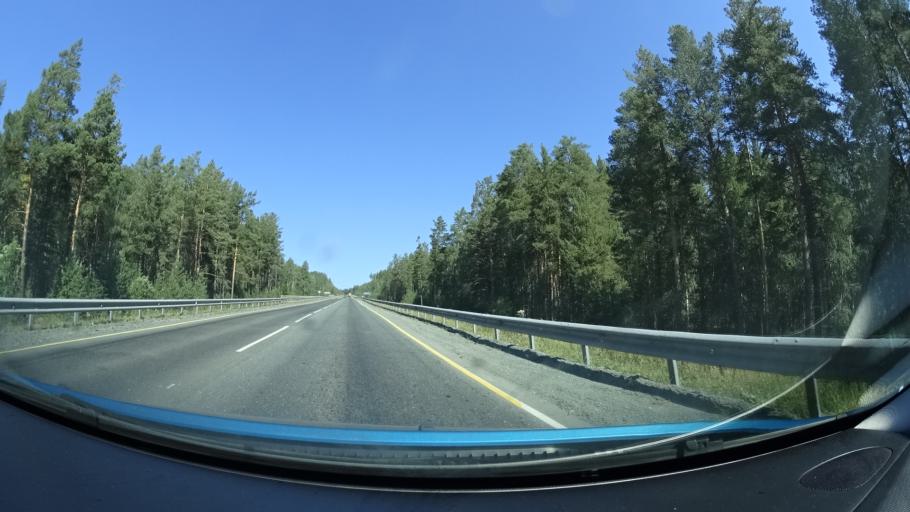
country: RU
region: Bashkortostan
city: Abzakovo
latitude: 53.8791
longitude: 58.5322
